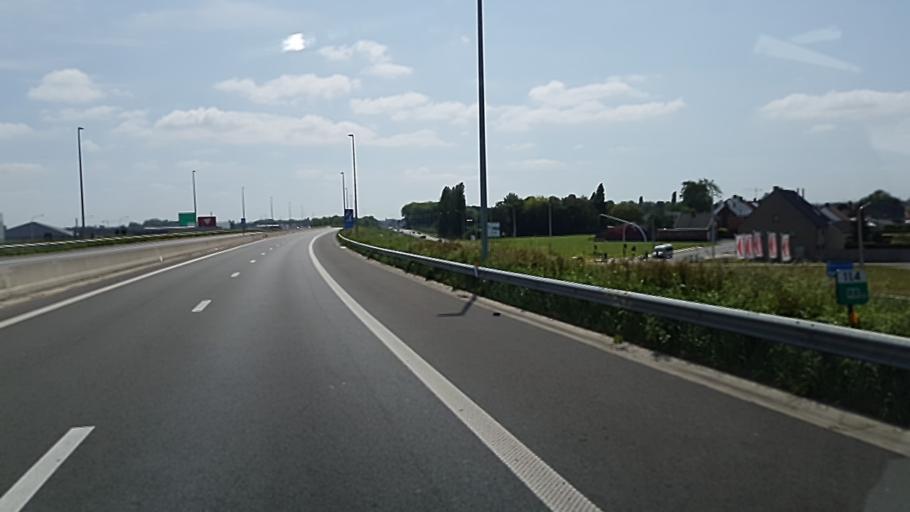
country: BE
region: Flanders
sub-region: Provincie West-Vlaanderen
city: Kortrijk
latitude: 50.8526
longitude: 3.2509
